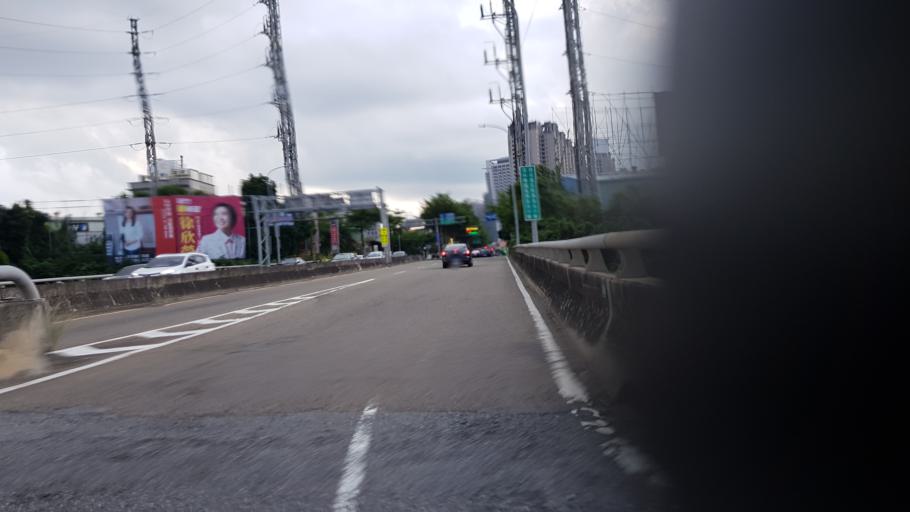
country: TW
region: Taiwan
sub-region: Hsinchu
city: Zhubei
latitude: 24.7990
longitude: 121.0134
